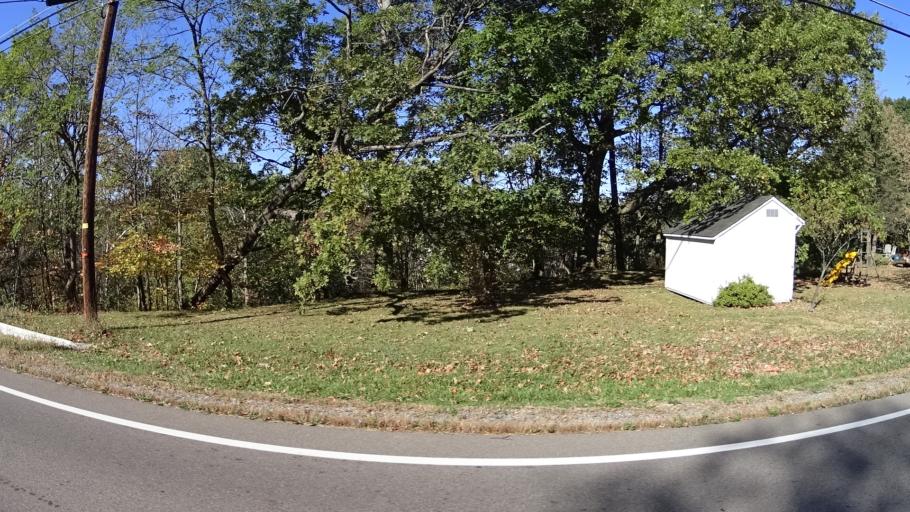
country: US
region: Ohio
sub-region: Lorain County
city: Amherst
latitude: 41.3881
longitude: -82.2312
